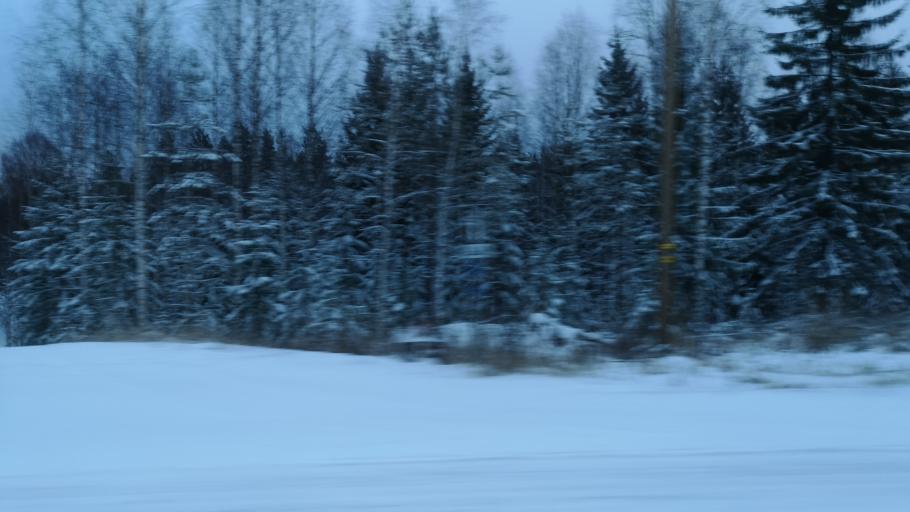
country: FI
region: Southern Savonia
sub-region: Savonlinna
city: Enonkoski
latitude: 62.0523
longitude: 28.7041
